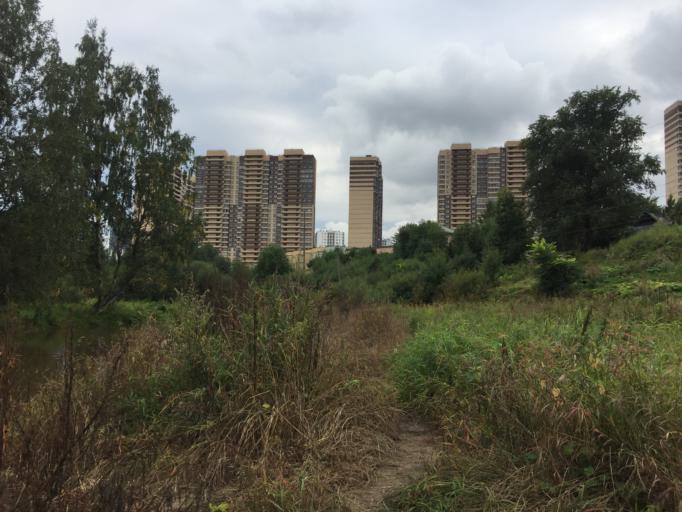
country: RU
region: Leningrad
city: Murino
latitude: 60.0420
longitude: 30.4572
